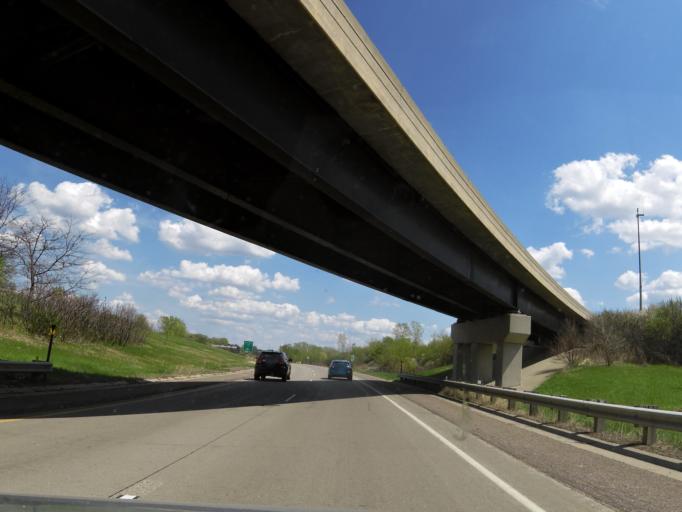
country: US
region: Minnesota
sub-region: Dakota County
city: Mendota Heights
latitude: 44.8822
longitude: -93.1655
